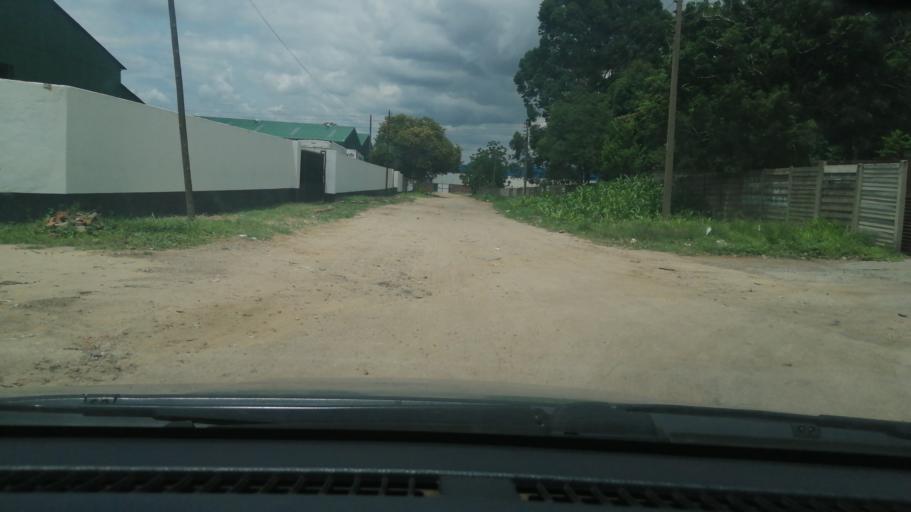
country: ZW
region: Harare
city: Harare
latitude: -17.8753
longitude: 31.0234
